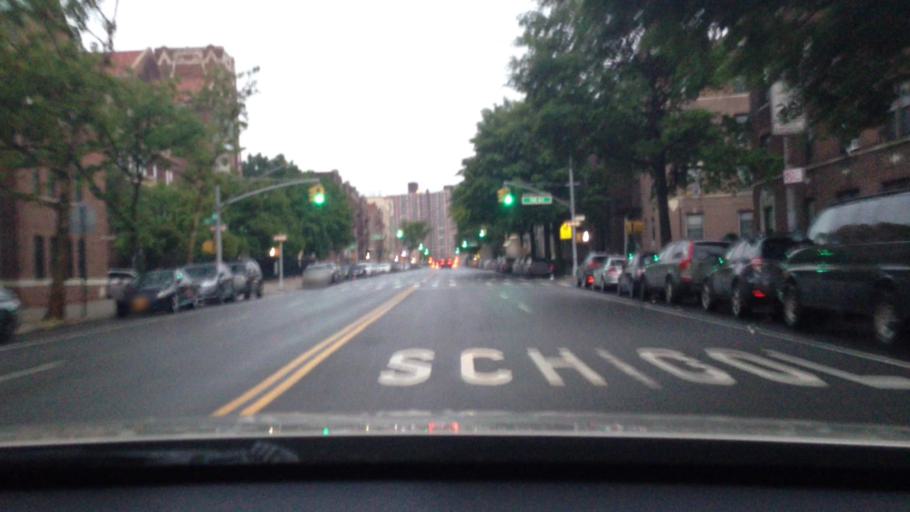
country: US
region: New York
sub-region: Kings County
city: Bensonhurst
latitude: 40.6310
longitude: -74.0250
